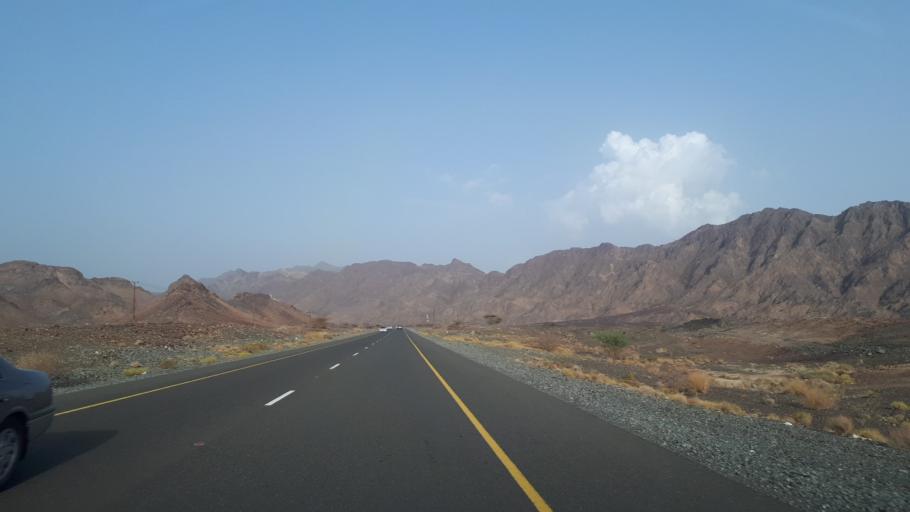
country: OM
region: Az Zahirah
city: Yanqul
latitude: 23.4958
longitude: 56.8572
